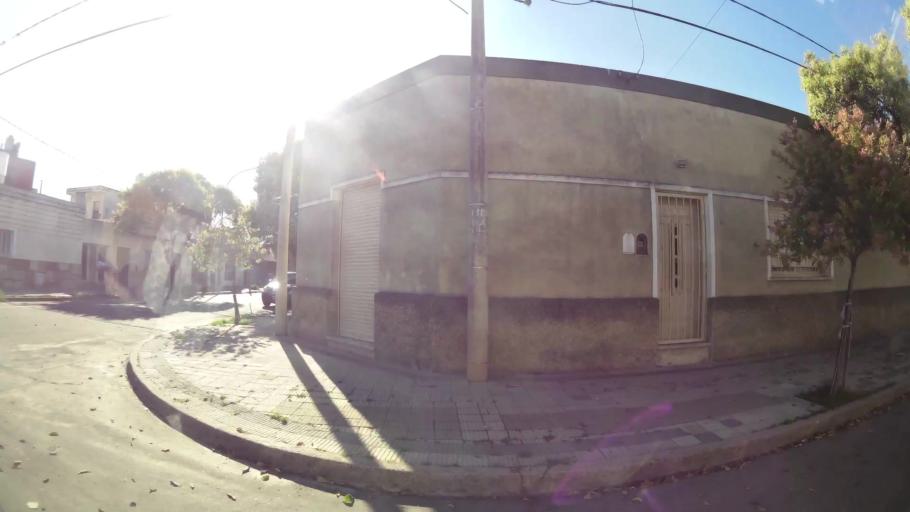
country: AR
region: Cordoba
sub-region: Departamento de Capital
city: Cordoba
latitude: -31.3937
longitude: -64.1687
